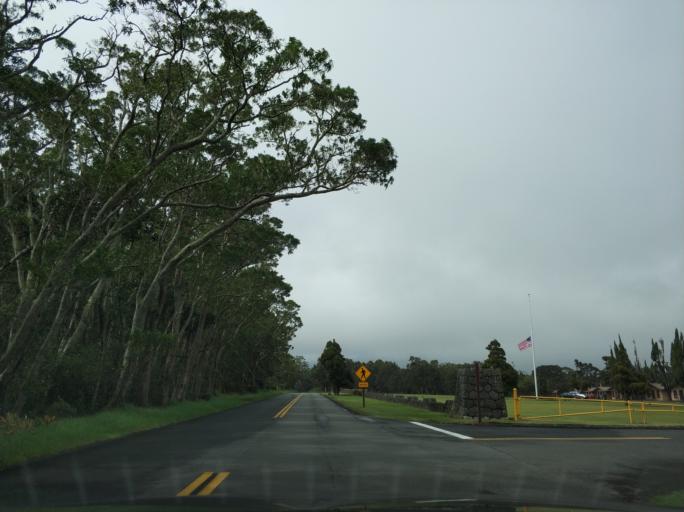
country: US
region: Hawaii
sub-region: Hawaii County
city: Volcano
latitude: 19.4320
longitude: -155.2731
